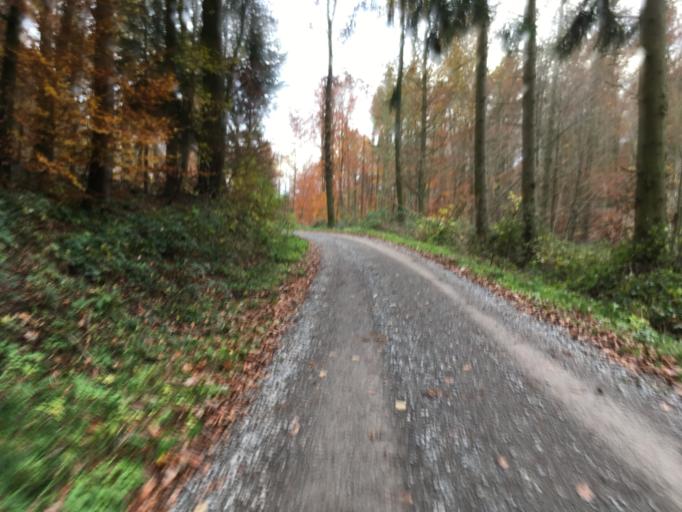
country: DE
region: Baden-Wuerttemberg
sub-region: Regierungsbezirk Stuttgart
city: Untergruppenbach
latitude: 49.0943
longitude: 9.2976
